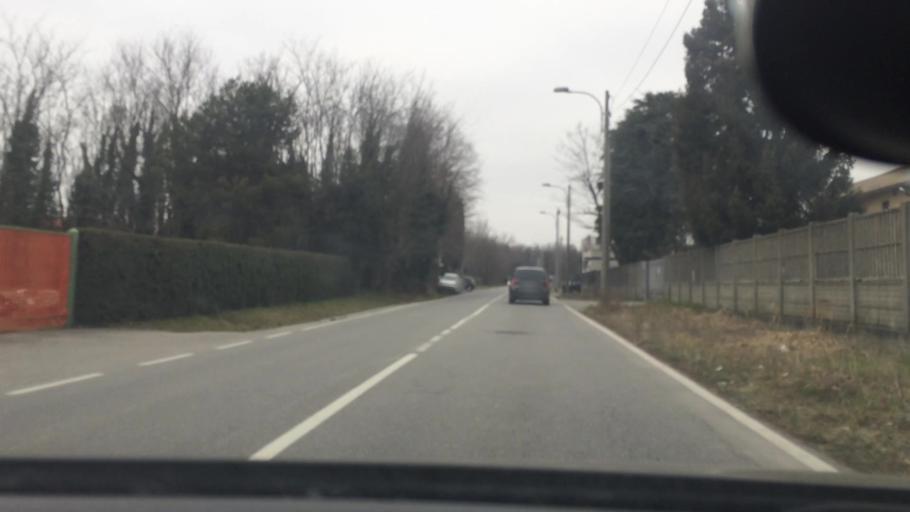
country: IT
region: Lombardy
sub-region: Provincia di Monza e Brianza
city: Cogliate
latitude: 45.6412
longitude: 9.1043
